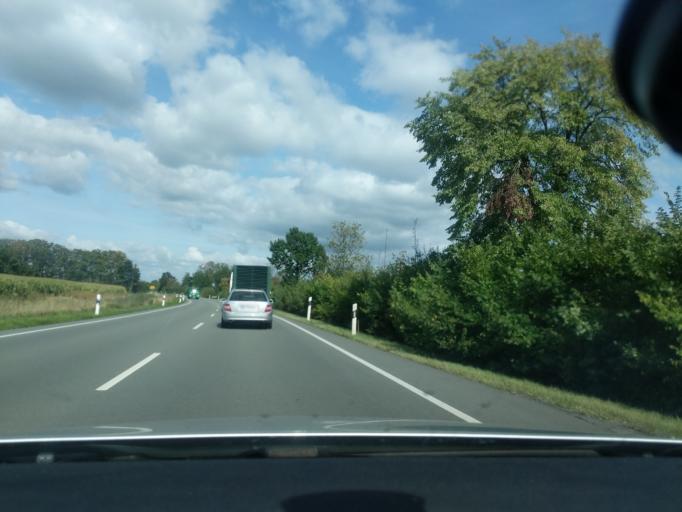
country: DE
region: Lower Saxony
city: Bohmte
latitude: 52.3609
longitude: 8.2993
